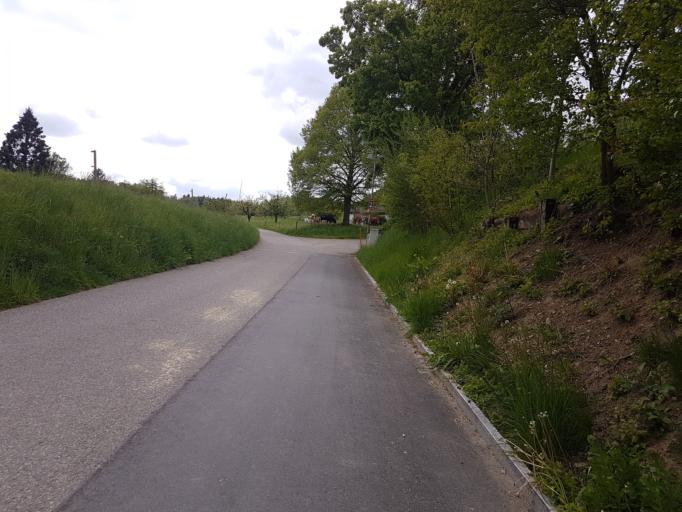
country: CH
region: Bern
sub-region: Seeland District
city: Leuzigen
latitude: 47.1839
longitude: 7.4922
